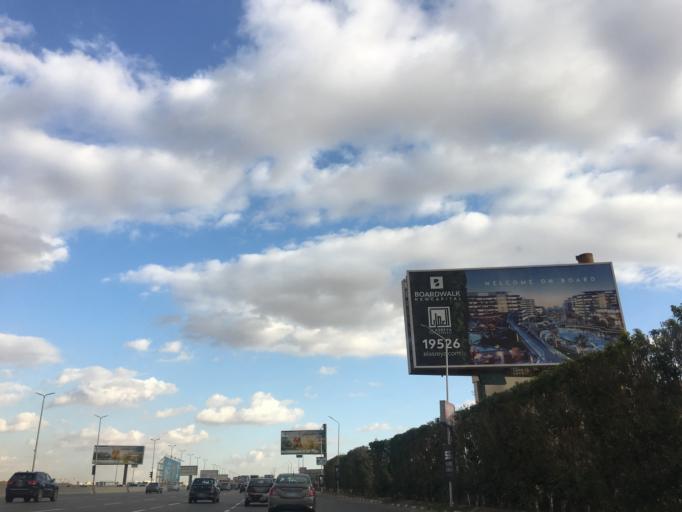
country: EG
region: Muhafazat al Qahirah
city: Cairo
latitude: 30.0211
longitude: 31.3750
